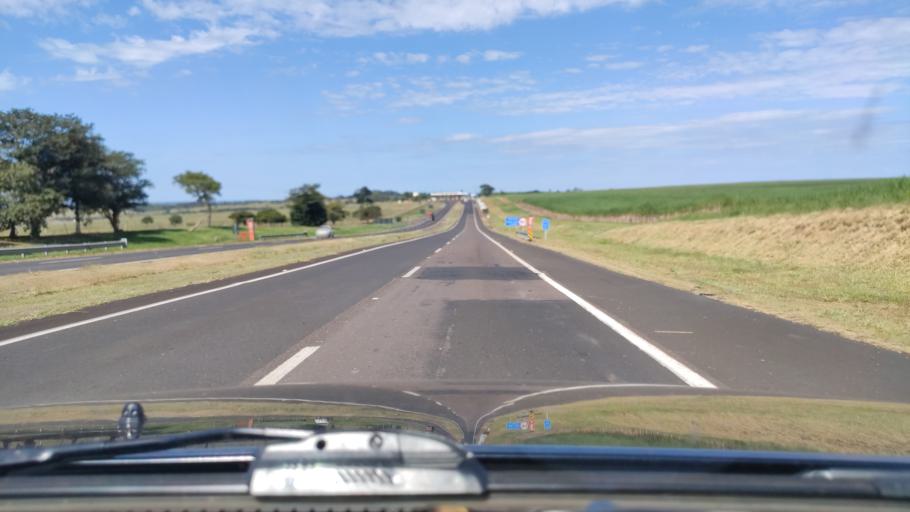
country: BR
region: Sao Paulo
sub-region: Rancharia
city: Rancharia
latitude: -22.4312
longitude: -51.0156
